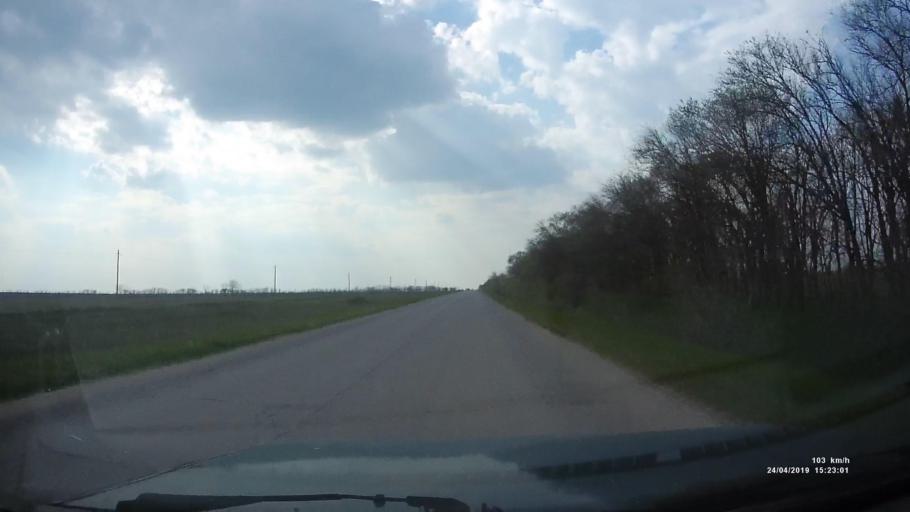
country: RU
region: Rostov
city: Remontnoye
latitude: 46.5415
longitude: 43.0985
